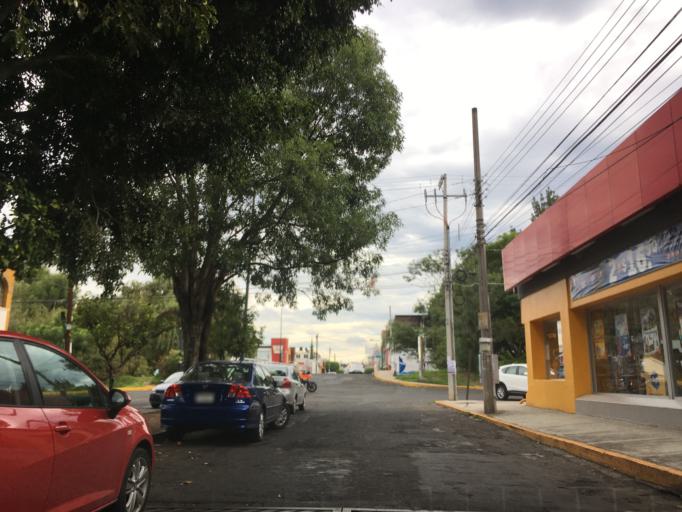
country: MX
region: Michoacan
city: Morelia
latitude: 19.6849
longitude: -101.1703
